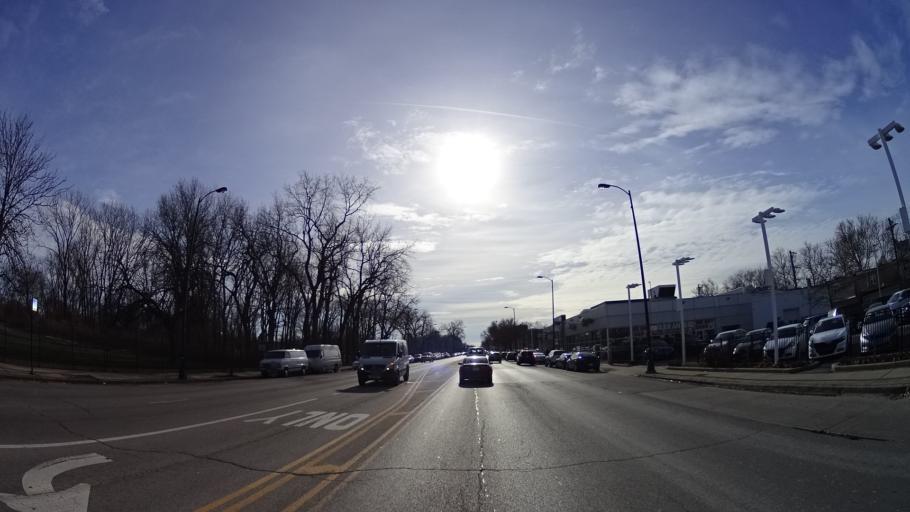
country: US
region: Illinois
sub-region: Cook County
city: Lincolnwood
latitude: 41.9904
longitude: -87.6898
